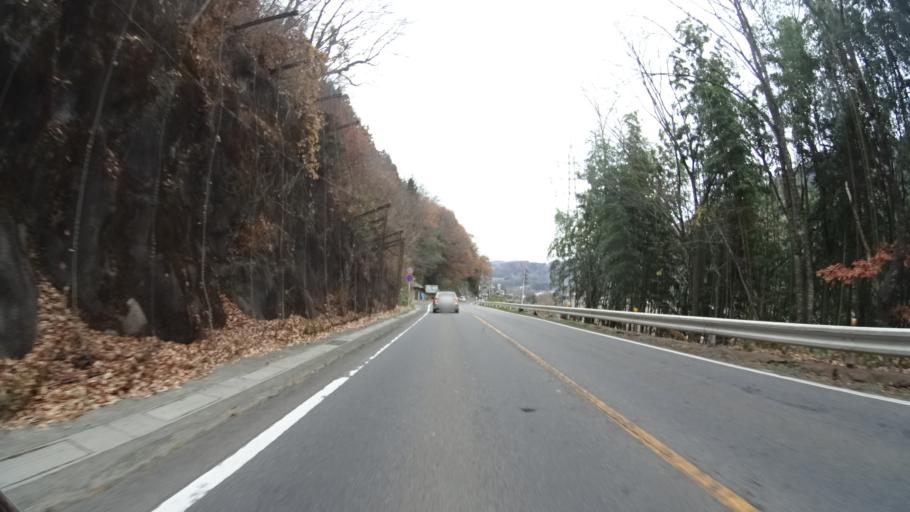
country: JP
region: Gunma
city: Numata
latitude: 36.6829
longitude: 139.2070
